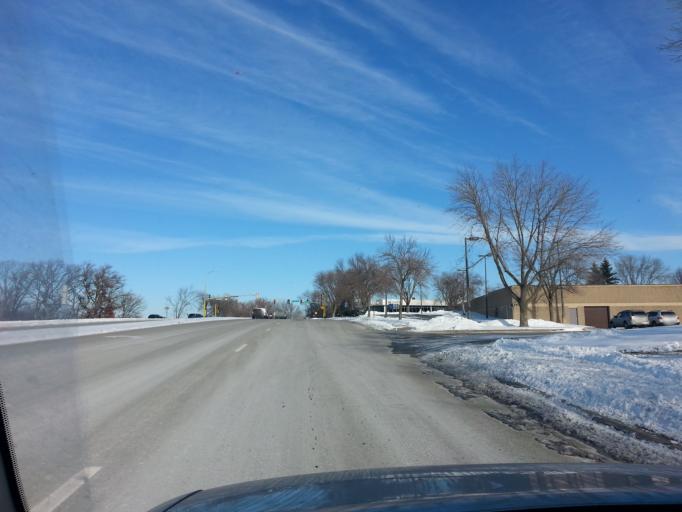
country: US
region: Minnesota
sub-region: Hennepin County
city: Edina
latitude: 44.8607
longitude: -93.3619
